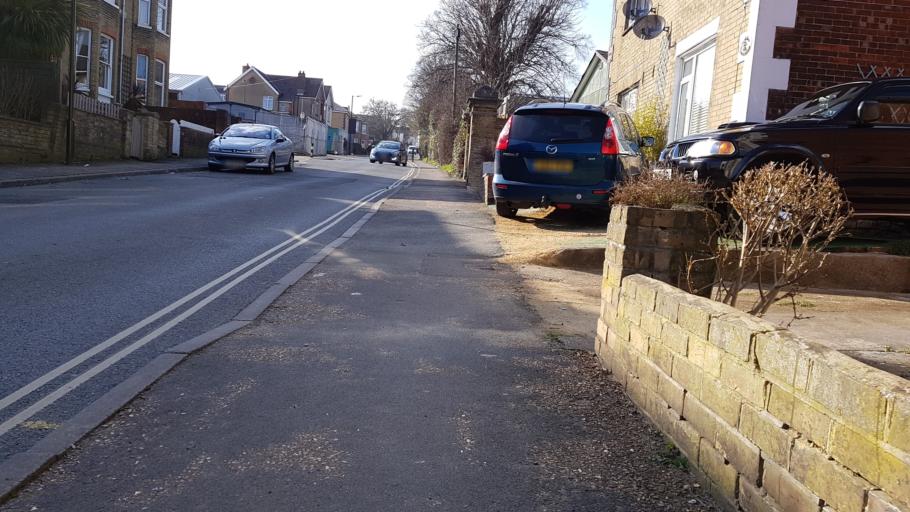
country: GB
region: England
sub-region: Isle of Wight
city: Ryde
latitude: 50.7266
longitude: -1.1566
